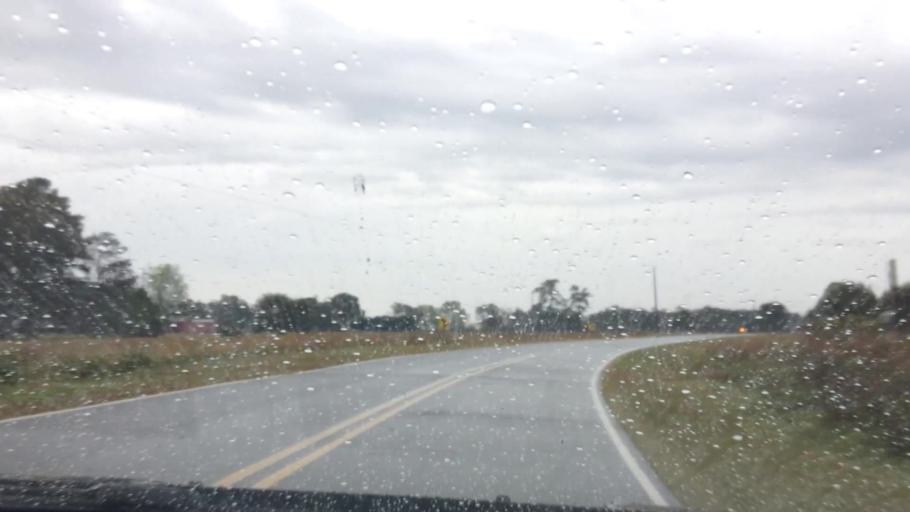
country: US
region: North Carolina
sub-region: Pitt County
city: Grifton
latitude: 35.3901
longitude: -77.4014
